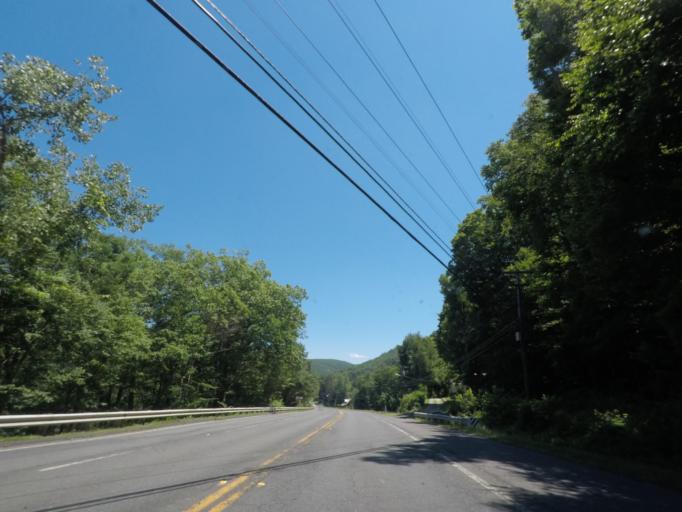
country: US
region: Massachusetts
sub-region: Hampden County
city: Granville
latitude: 42.1840
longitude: -72.8526
